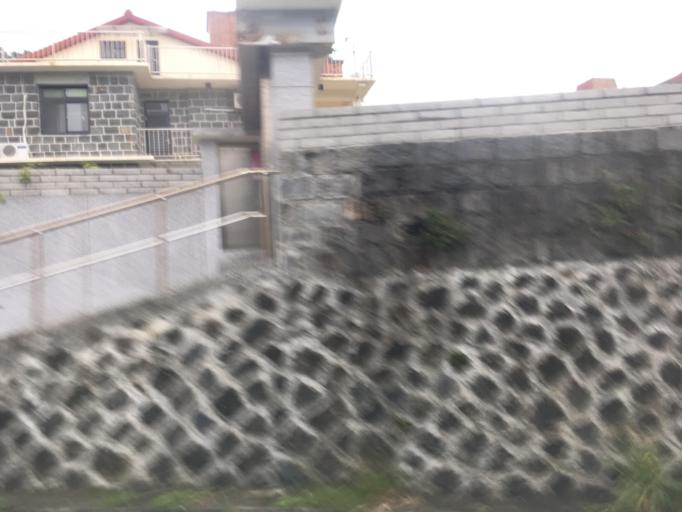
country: TW
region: Taipei
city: Taipei
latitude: 25.1316
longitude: 121.5282
